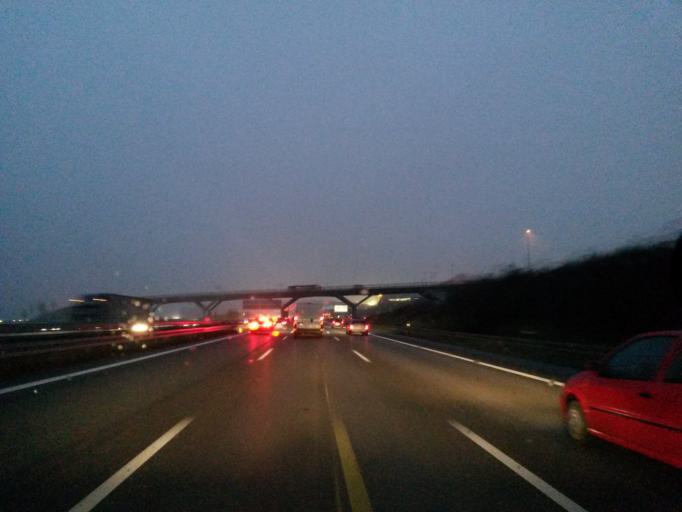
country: DE
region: Baden-Wuerttemberg
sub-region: Regierungsbezirk Stuttgart
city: Leinfelden-Echterdingen
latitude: 48.6990
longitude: 9.1850
